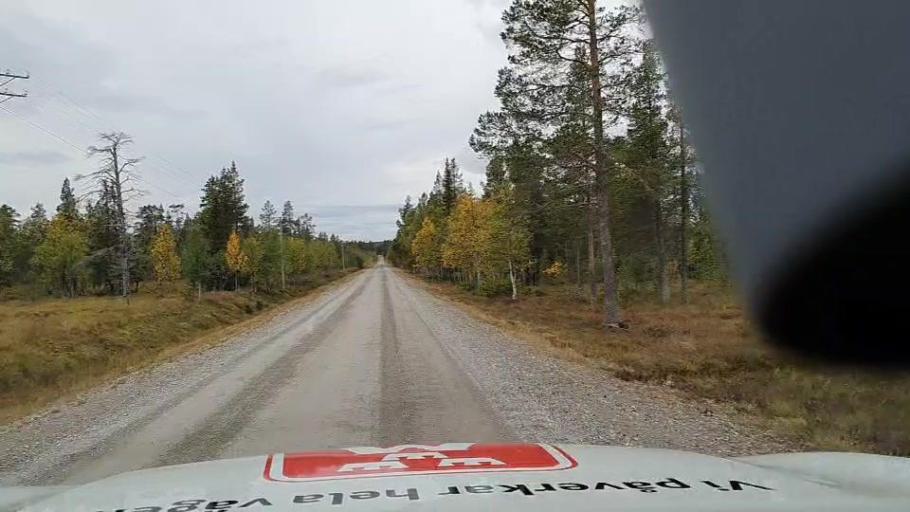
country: NO
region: Hedmark
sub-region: Engerdal
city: Engerdal
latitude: 62.0930
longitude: 12.8001
